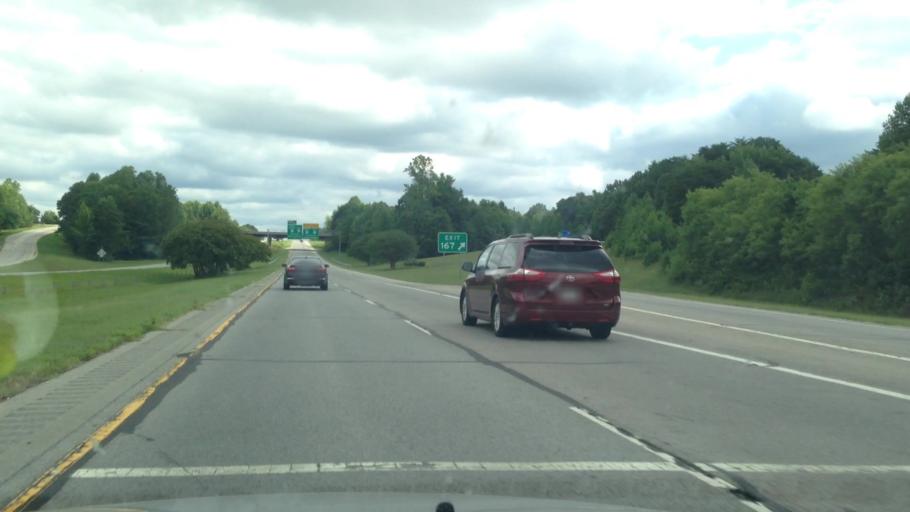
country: US
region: Virginia
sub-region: City of Danville
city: Danville
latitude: 36.5152
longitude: -79.4757
